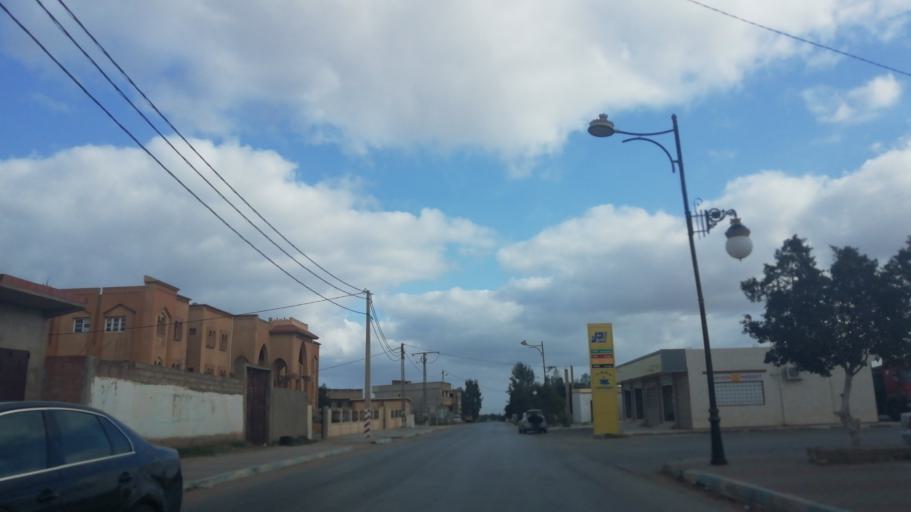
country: DZ
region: Relizane
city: Mazouna
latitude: 36.2738
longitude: 0.6343
